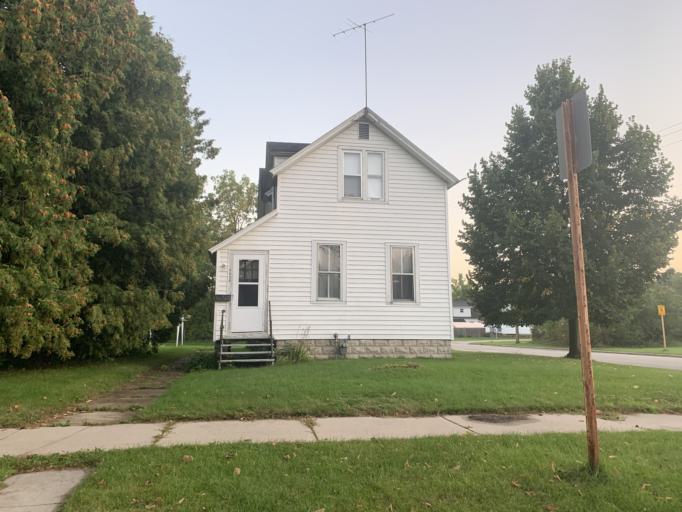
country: US
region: Wisconsin
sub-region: Marinette County
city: Marinette
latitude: 45.0983
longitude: -87.6458
